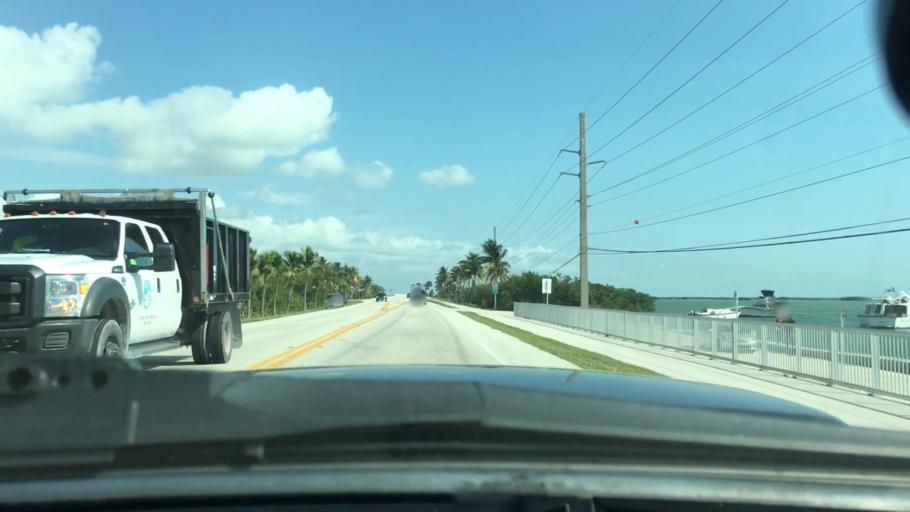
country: US
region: Florida
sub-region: Monroe County
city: Big Coppitt Key
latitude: 24.6015
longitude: -81.6471
